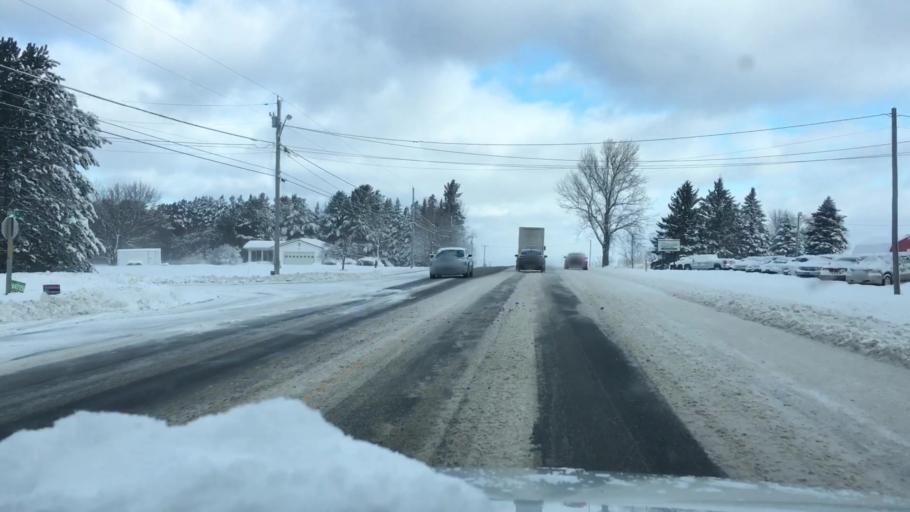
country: US
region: Maine
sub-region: Aroostook County
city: Caribou
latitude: 46.7921
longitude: -67.9912
